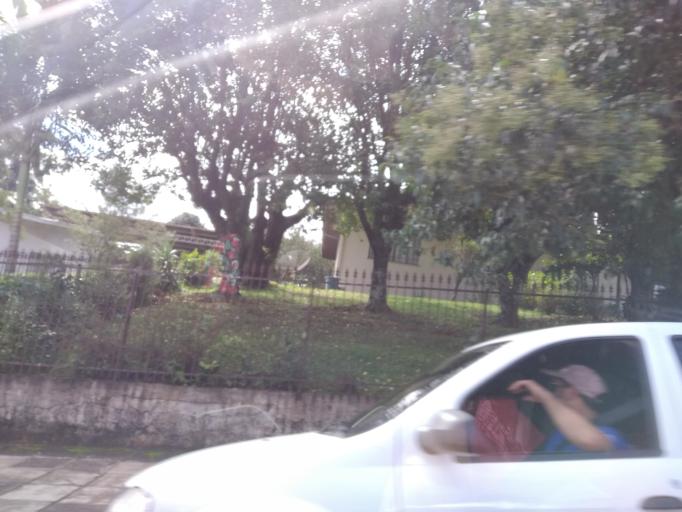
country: BR
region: Parana
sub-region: Pato Branco
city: Pato Branco
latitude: -26.2300
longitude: -52.6654
